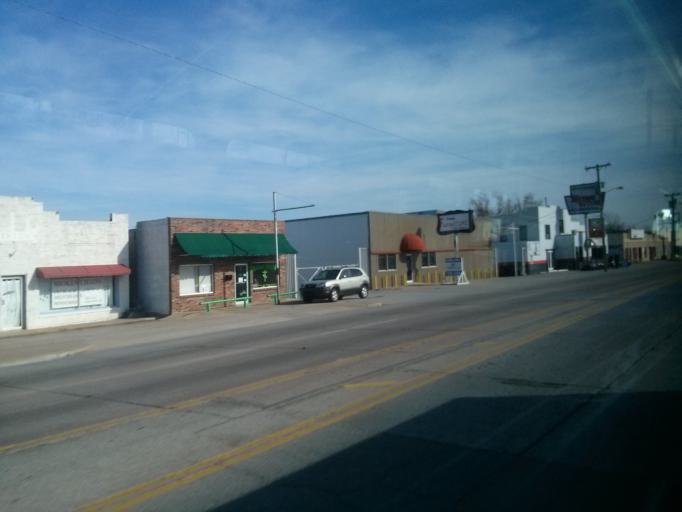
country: US
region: Oklahoma
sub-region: Tulsa County
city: Tulsa
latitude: 36.1607
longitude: -95.9214
